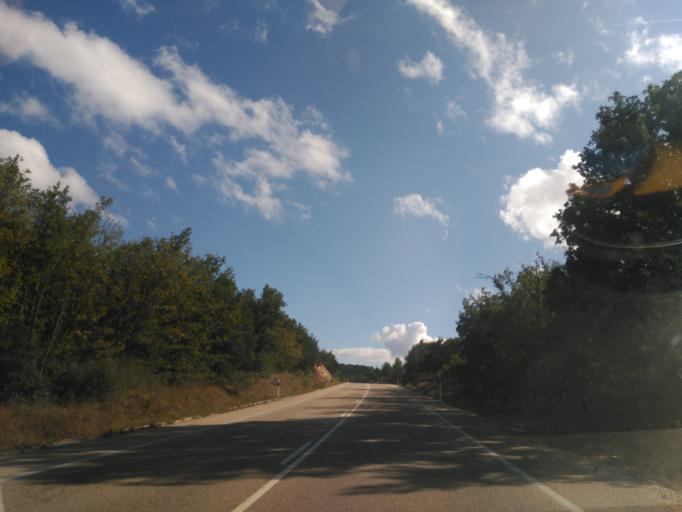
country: ES
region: Castille and Leon
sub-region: Provincia de Burgos
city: Pinilla de los Barruecos
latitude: 41.9184
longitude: -3.2795
